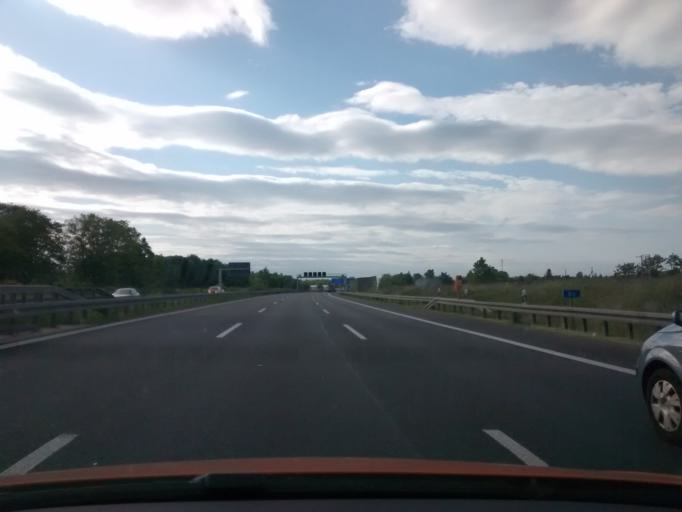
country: DE
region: Brandenburg
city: Schonefeld
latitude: 52.3866
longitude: 13.5311
